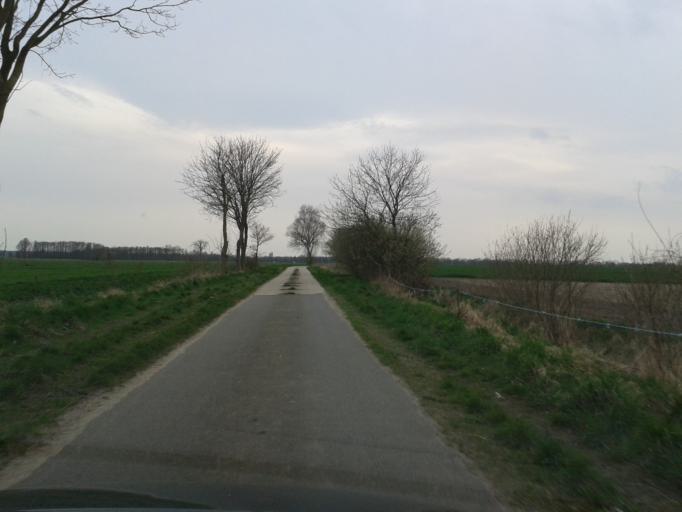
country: DE
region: Lower Saxony
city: Prezelle
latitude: 52.9026
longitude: 11.3389
